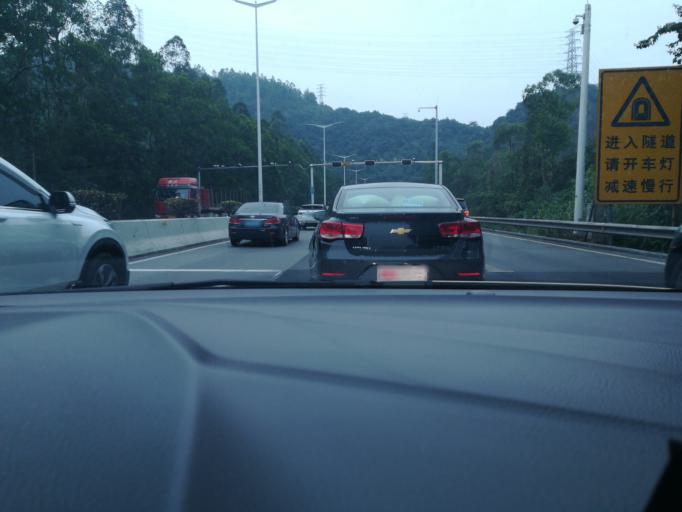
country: CN
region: Guangdong
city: Longdong
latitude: 23.2257
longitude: 113.3564
